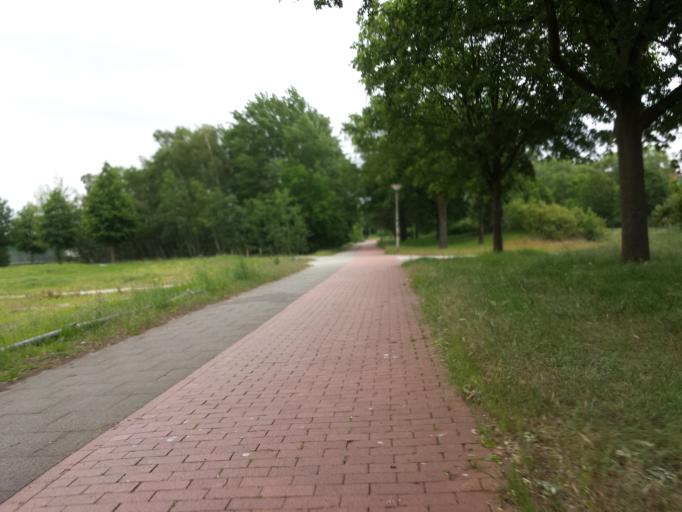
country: DE
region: Bremen
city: Bremen
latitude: 53.1052
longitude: 8.8576
